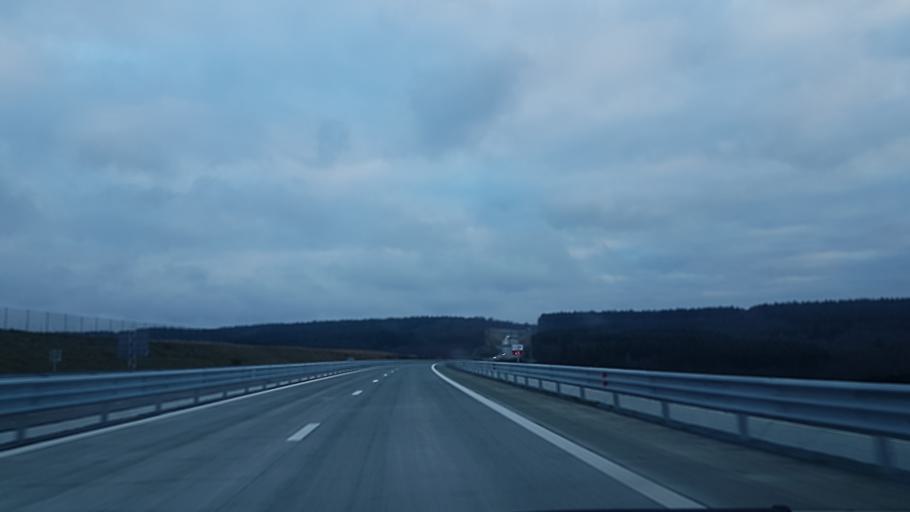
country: BE
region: Wallonia
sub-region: Province de Namur
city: Couvin
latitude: 50.0136
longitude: 4.5338
